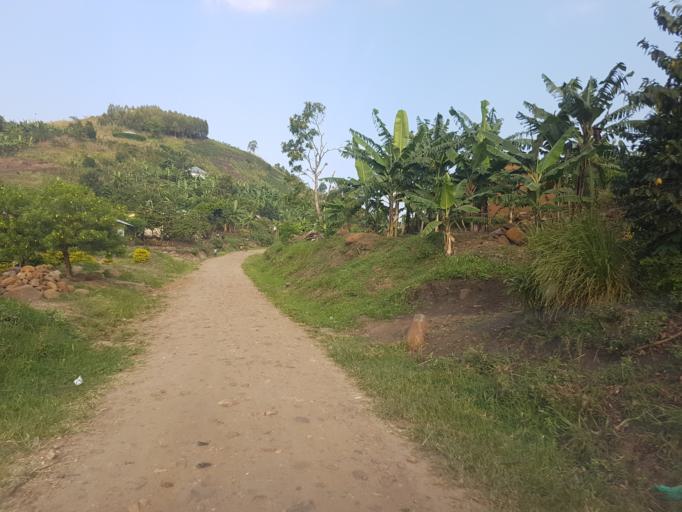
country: UG
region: Western Region
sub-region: Mitoma District
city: Mitoma
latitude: -0.6774
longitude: 29.9029
